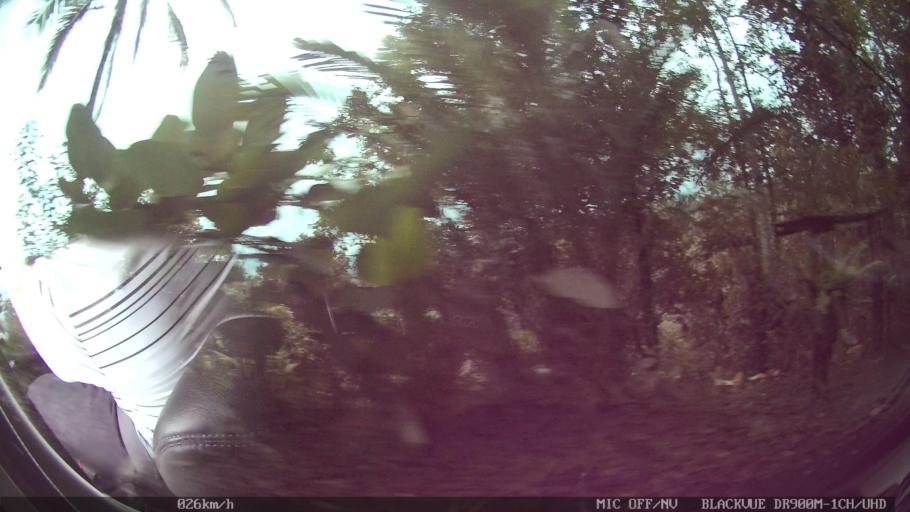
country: ID
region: Bali
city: Peneng
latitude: -8.3597
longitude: 115.2061
